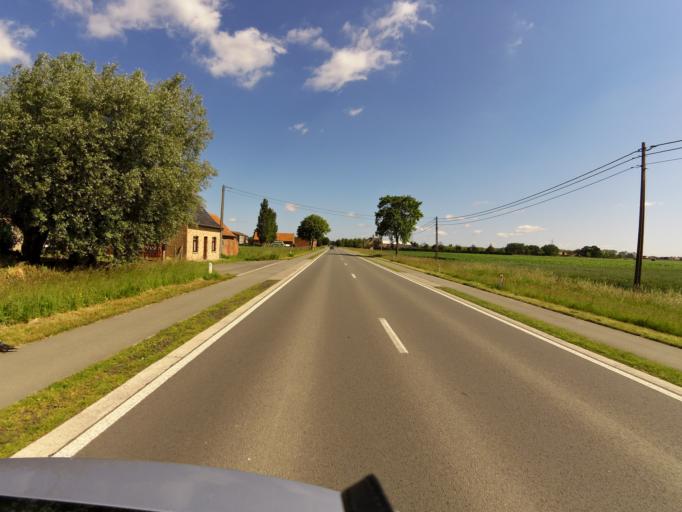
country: BE
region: Flanders
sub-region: Provincie West-Vlaanderen
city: Diksmuide
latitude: 50.9653
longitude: 2.8682
